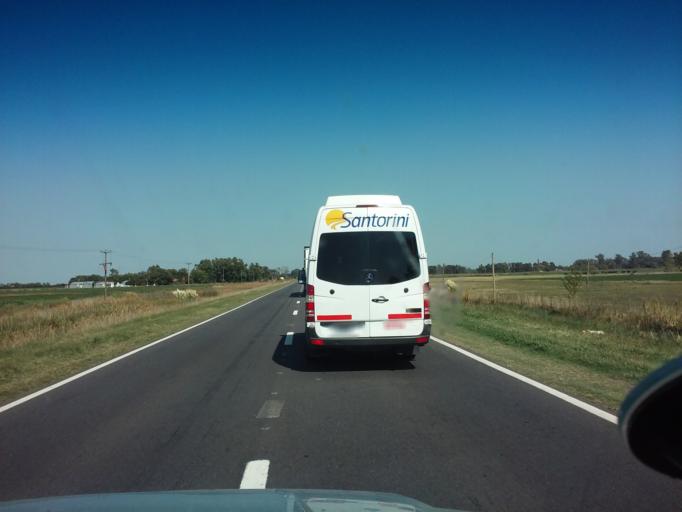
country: AR
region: Buenos Aires
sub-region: Partido de Chivilcoy
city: Chivilcoy
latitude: -34.9569
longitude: -60.0292
